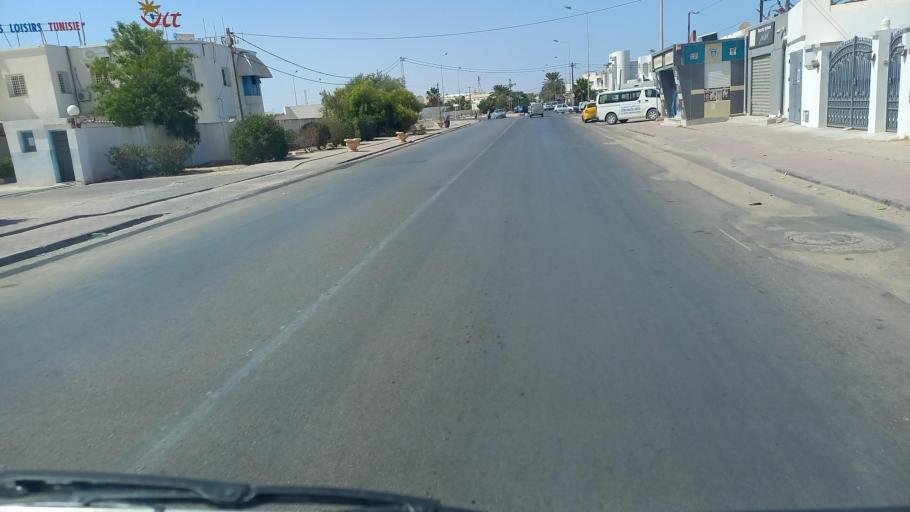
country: TN
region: Madanin
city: Houmt Souk
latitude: 33.8693
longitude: 10.8698
